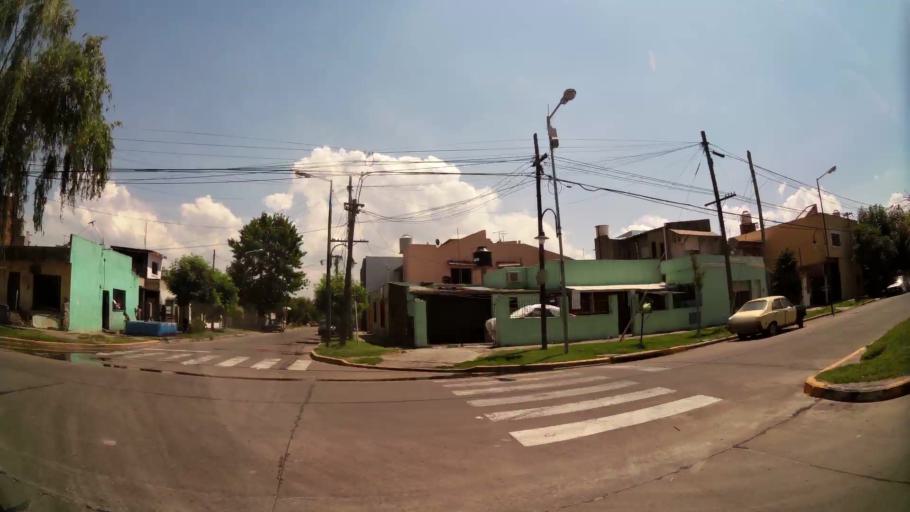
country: AR
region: Buenos Aires
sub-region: Partido de Tigre
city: Tigre
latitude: -34.4517
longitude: -58.5762
